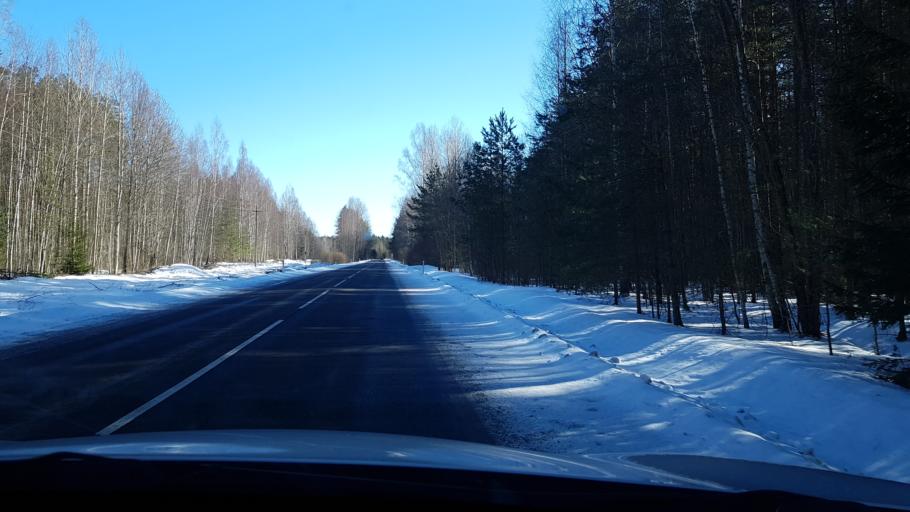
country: EE
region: Polvamaa
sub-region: Raepina vald
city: Rapina
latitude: 57.9968
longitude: 27.5513
